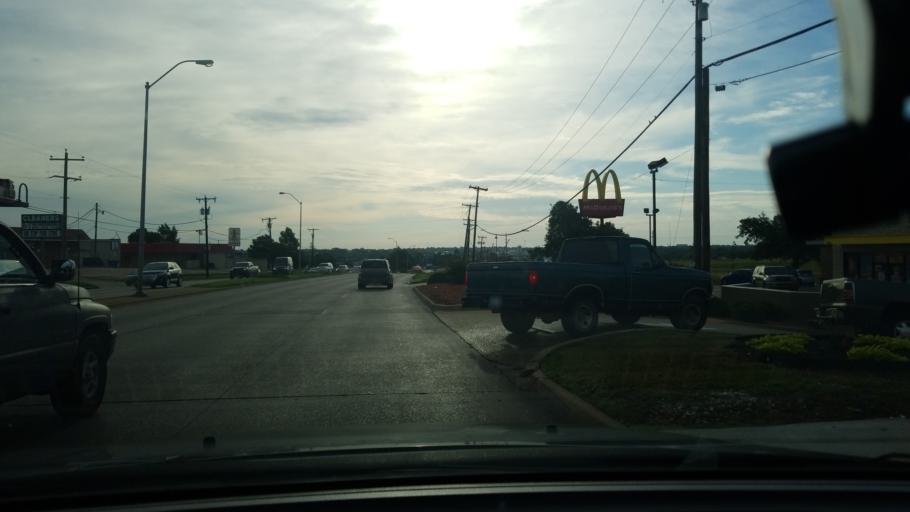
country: US
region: Texas
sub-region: Dallas County
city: Mesquite
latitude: 32.7668
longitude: -96.6296
